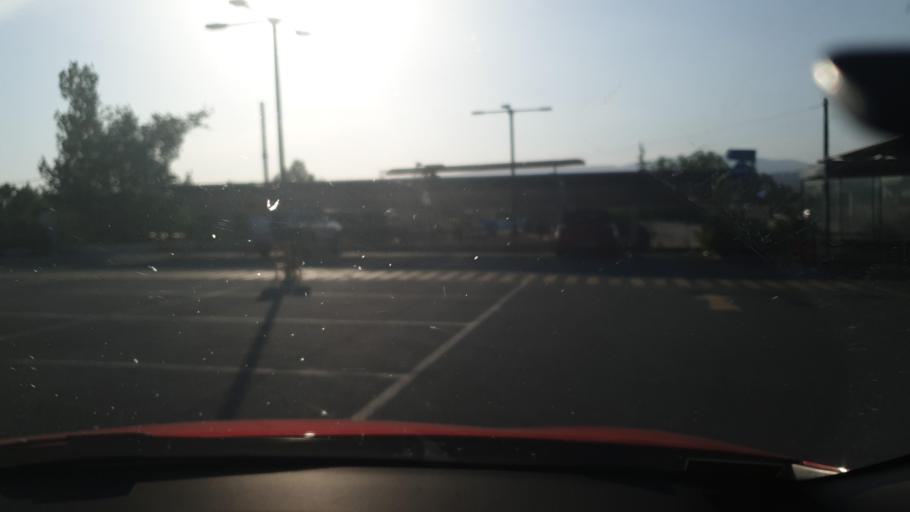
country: GR
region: Central Greece
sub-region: Nomos Evvoias
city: Aliveri
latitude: 38.4002
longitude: 24.0576
